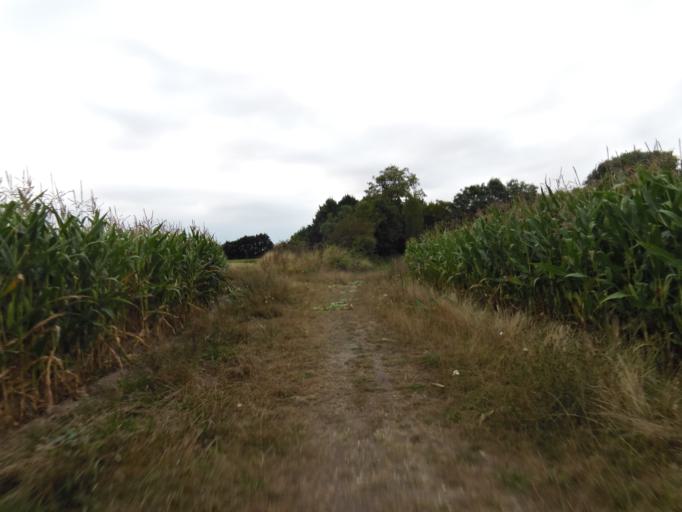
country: GB
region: England
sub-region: Hertfordshire
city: Radlett
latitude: 51.7199
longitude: -0.3170
